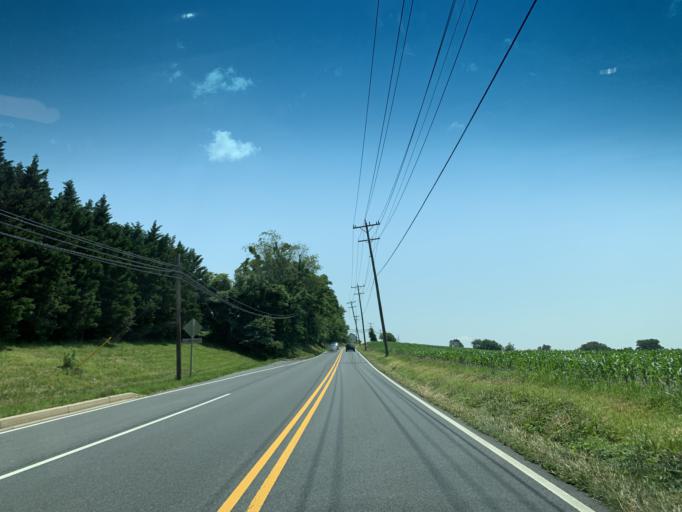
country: US
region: Maryland
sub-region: Frederick County
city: Green Valley
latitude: 39.3539
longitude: -77.2699
